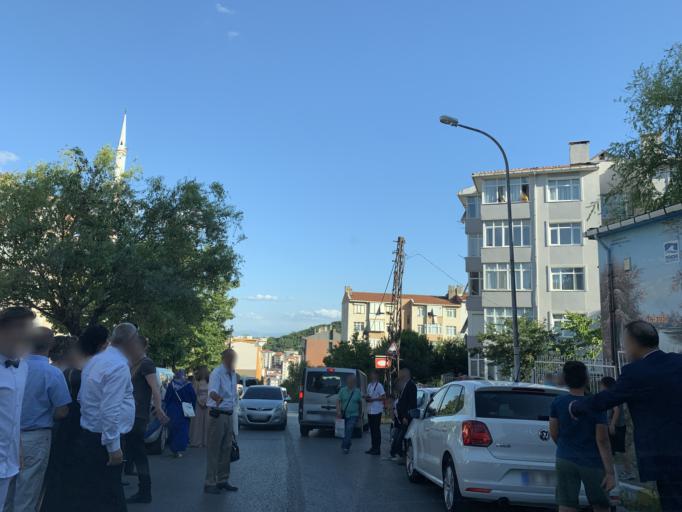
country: TR
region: Istanbul
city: Pendik
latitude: 40.8987
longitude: 29.2490
